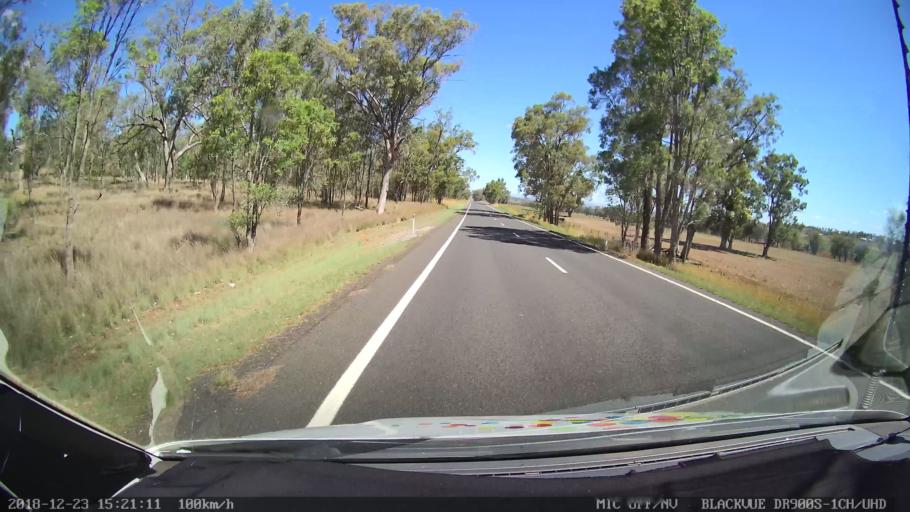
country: AU
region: New South Wales
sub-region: Tamworth Municipality
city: Manilla
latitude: -30.8529
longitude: 150.7949
